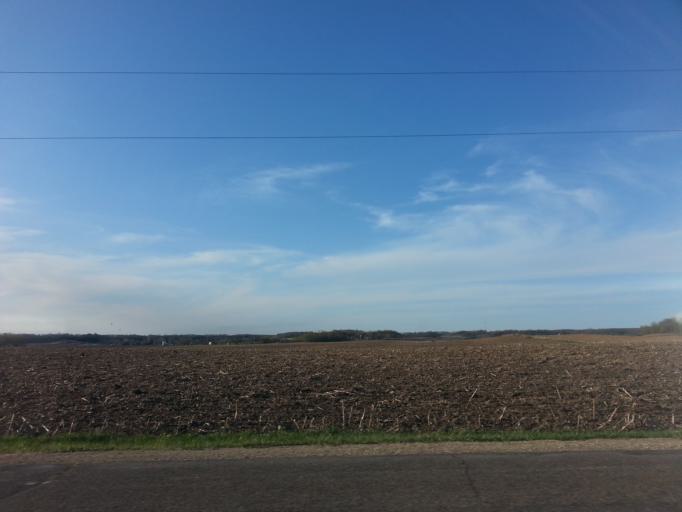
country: US
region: Wisconsin
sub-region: Pierce County
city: River Falls
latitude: 44.8624
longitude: -92.7070
